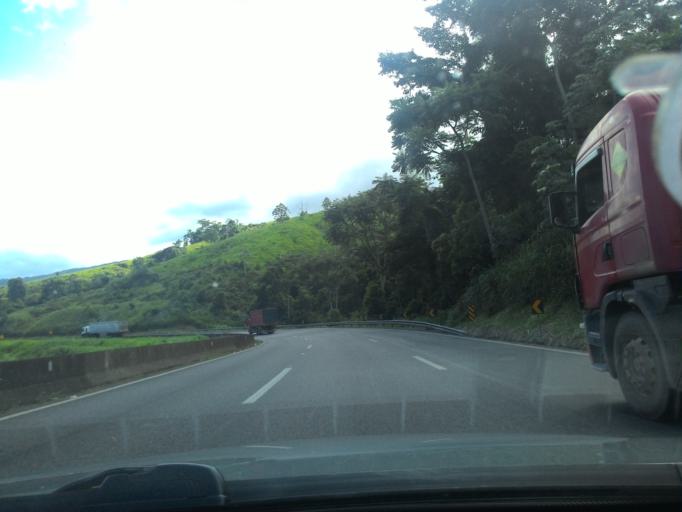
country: BR
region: Sao Paulo
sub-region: Cajati
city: Cajati
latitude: -24.7884
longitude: -48.2097
